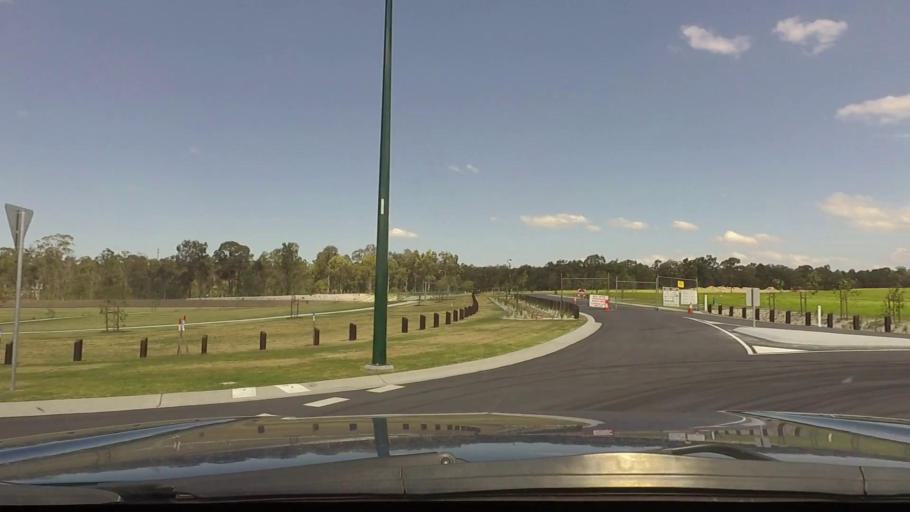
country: AU
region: Queensland
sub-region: Logan
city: North Maclean
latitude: -27.7376
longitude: 152.9512
